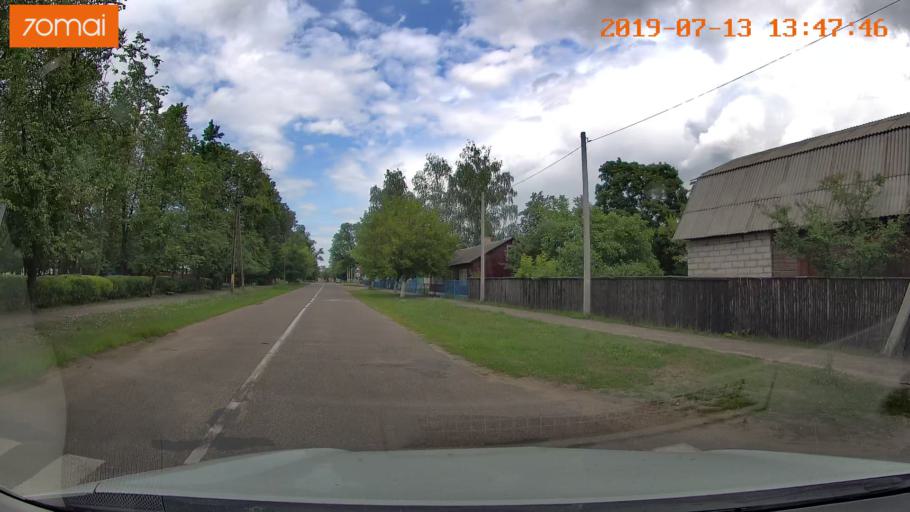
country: BY
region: Mogilev
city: Asipovichy
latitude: 53.2966
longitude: 28.6407
